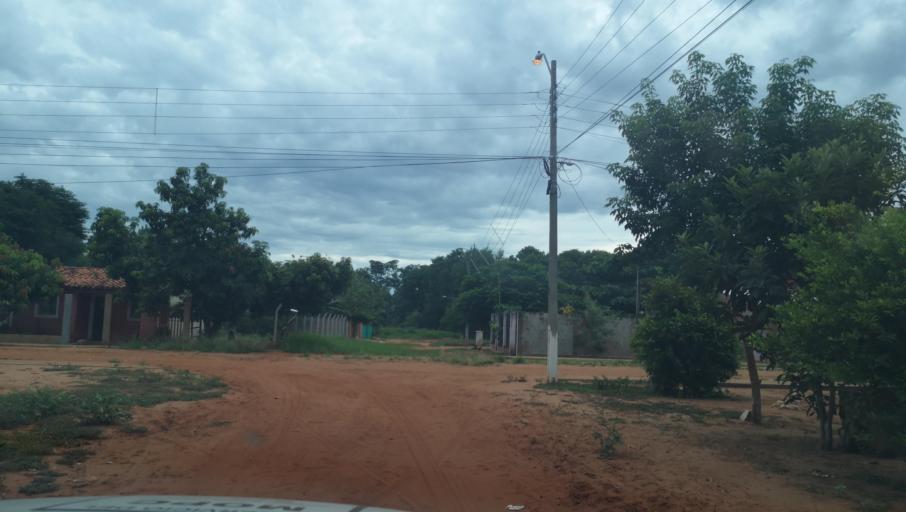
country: PY
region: San Pedro
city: Capiibary
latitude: -24.7434
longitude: -56.0321
